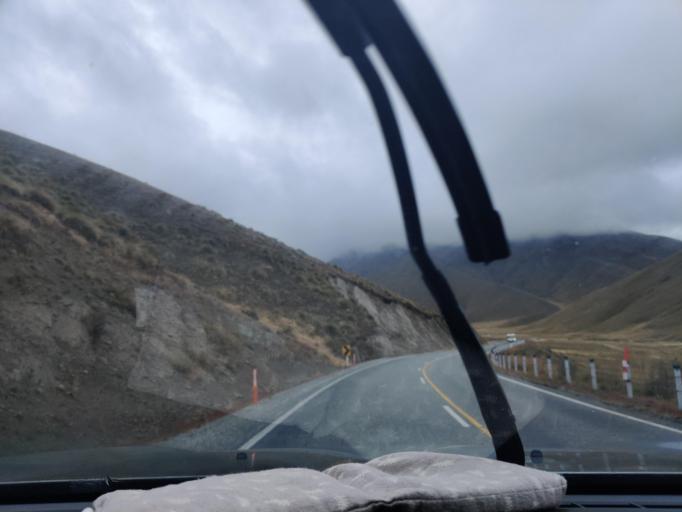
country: NZ
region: Otago
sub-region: Queenstown-Lakes District
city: Wanaka
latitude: -44.5833
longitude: 169.6368
